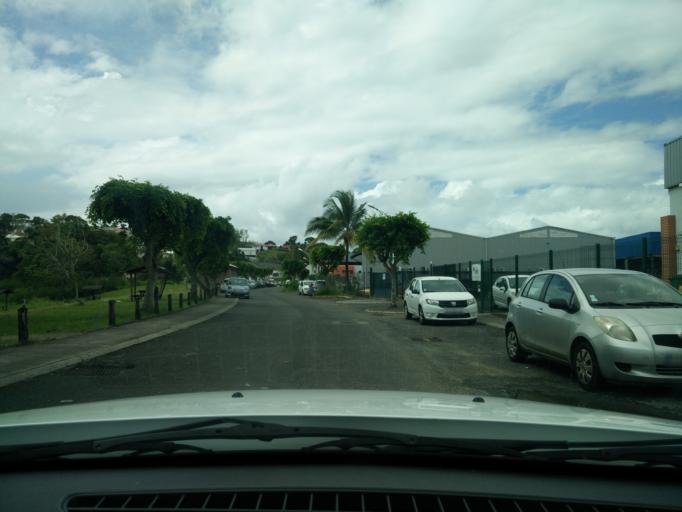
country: GP
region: Guadeloupe
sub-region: Guadeloupe
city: Petit-Bourg
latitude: 16.2008
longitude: -61.6089
